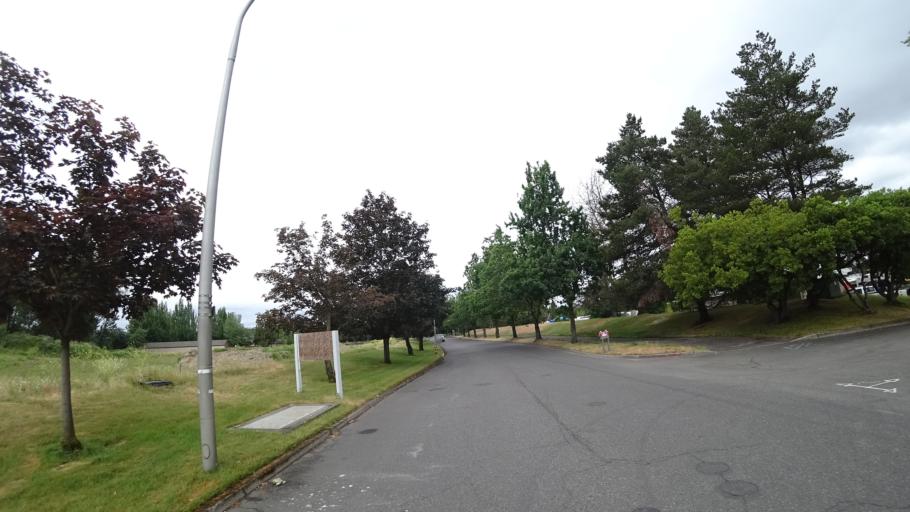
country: US
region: Washington
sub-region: Clark County
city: Vancouver
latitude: 45.6055
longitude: -122.6659
